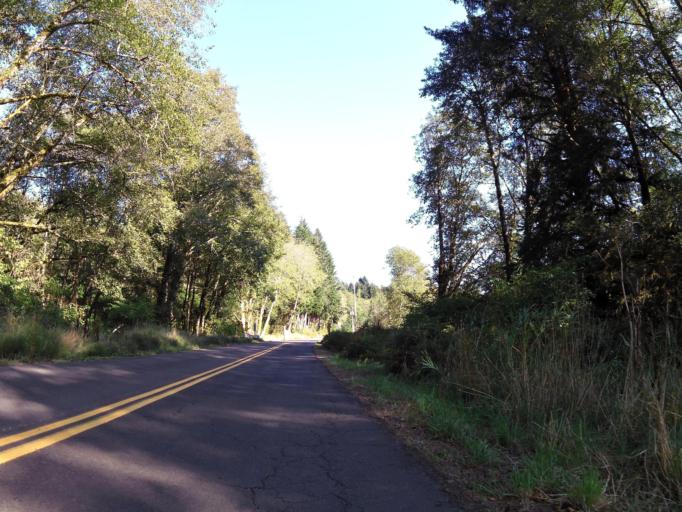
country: US
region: Oregon
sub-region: Lincoln County
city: Rose Lodge
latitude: 45.0746
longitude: -123.9271
